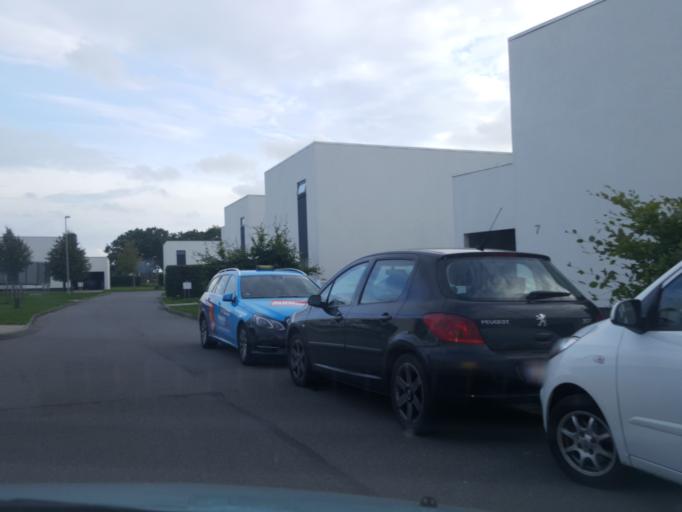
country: DK
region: South Denmark
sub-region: Fredericia Kommune
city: Taulov
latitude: 55.5367
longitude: 9.6286
